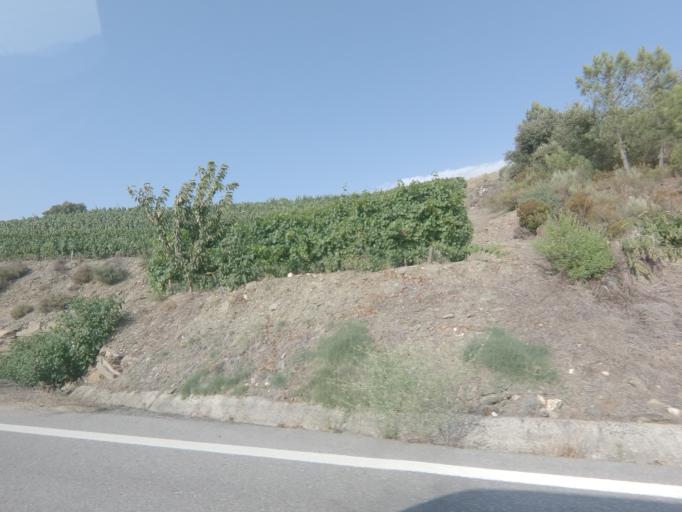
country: PT
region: Viseu
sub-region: Tabuaco
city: Tabuaco
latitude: 41.1449
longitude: -7.5449
